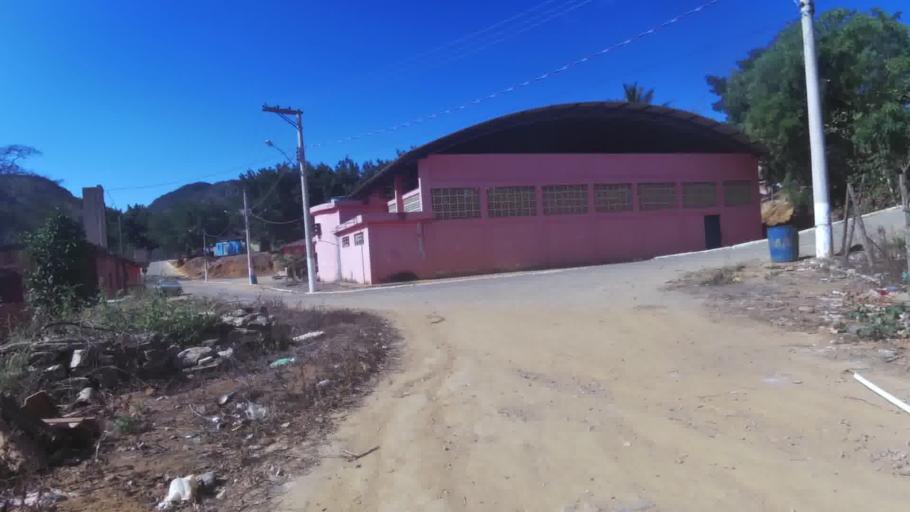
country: BR
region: Espirito Santo
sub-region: Cachoeiro De Itapemirim
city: Cachoeiro de Itapemirim
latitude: -20.9206
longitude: -41.1970
